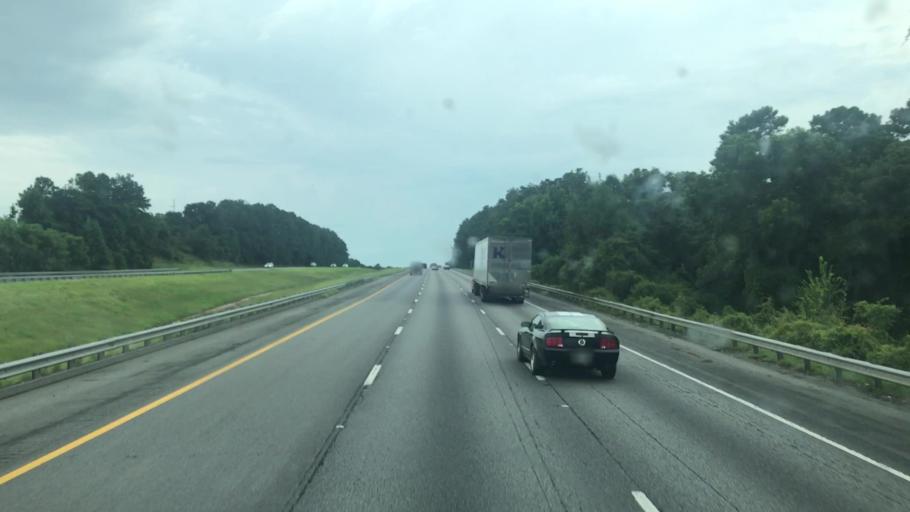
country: US
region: Georgia
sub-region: Houston County
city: Perry
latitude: 32.5287
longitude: -83.7439
